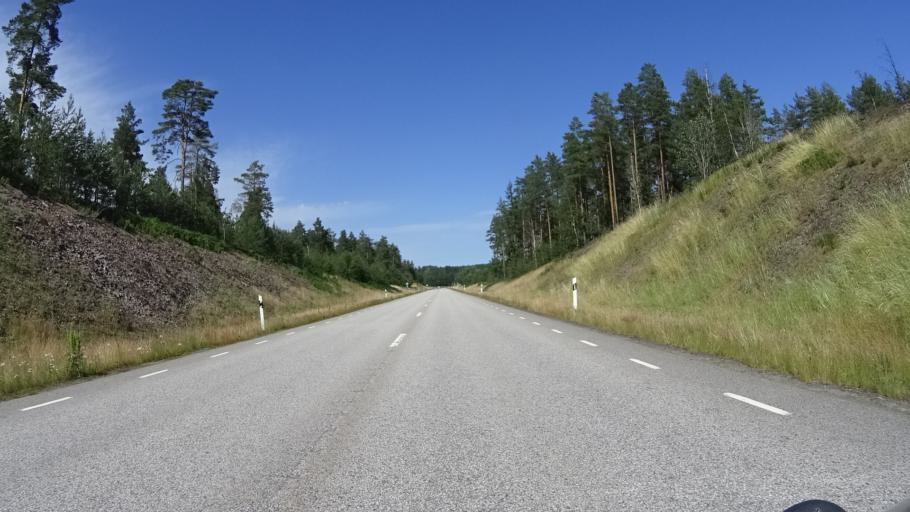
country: SE
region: Kalmar
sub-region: Vasterviks Kommun
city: Gamleby
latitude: 57.9324
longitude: 16.3796
